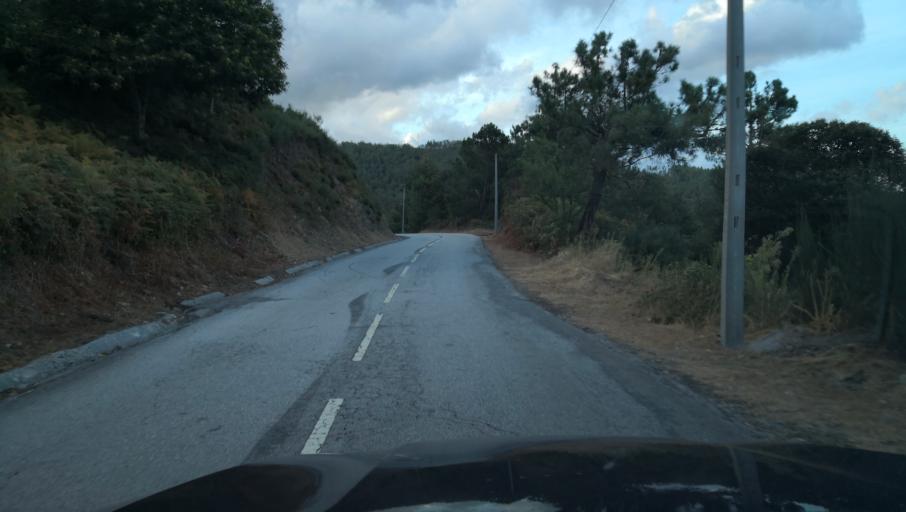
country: PT
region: Vila Real
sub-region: Santa Marta de Penaguiao
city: Santa Marta de Penaguiao
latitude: 41.2385
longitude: -7.8503
